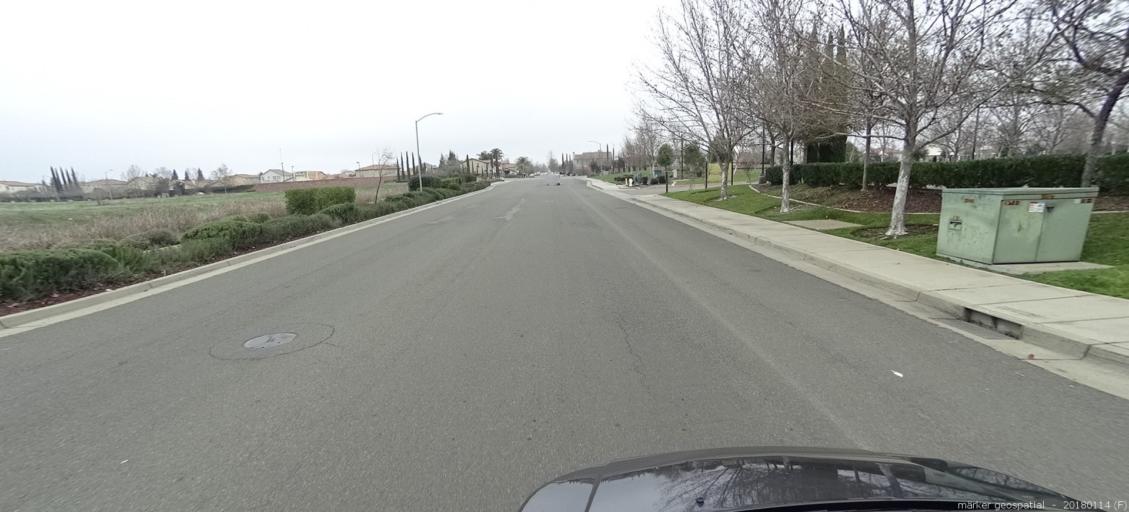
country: US
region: California
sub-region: Sacramento County
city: Rancho Cordova
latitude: 38.5468
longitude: -121.2386
